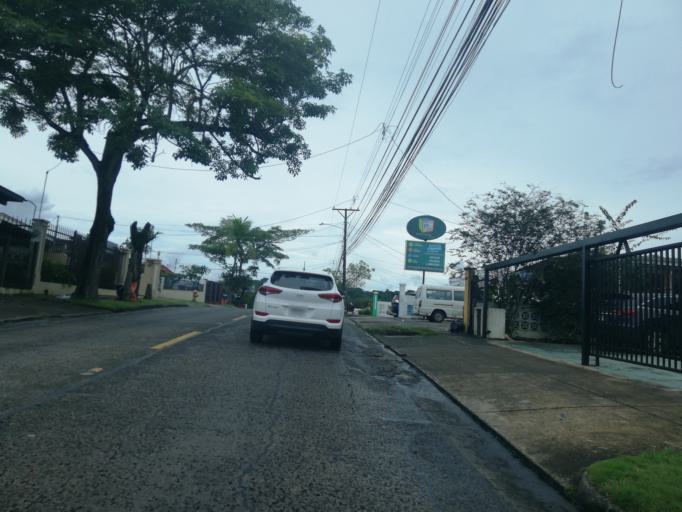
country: PA
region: Panama
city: Panama
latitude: 9.0108
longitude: -79.5395
